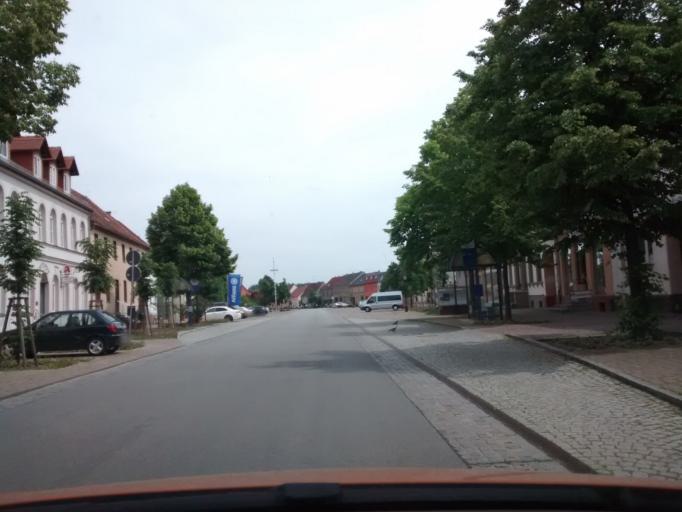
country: DE
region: Saxony-Anhalt
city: Holzdorf
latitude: 51.8145
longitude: 13.2261
